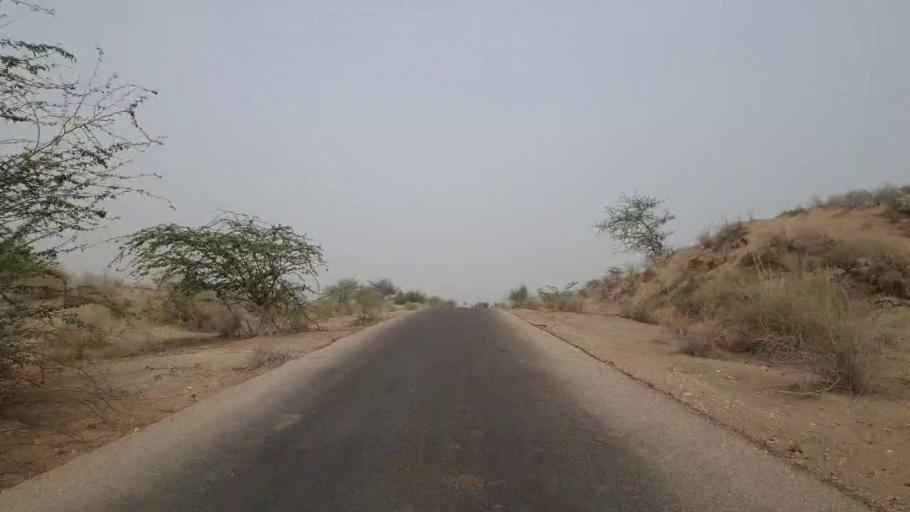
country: PK
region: Sindh
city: Islamkot
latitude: 24.5865
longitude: 70.2943
